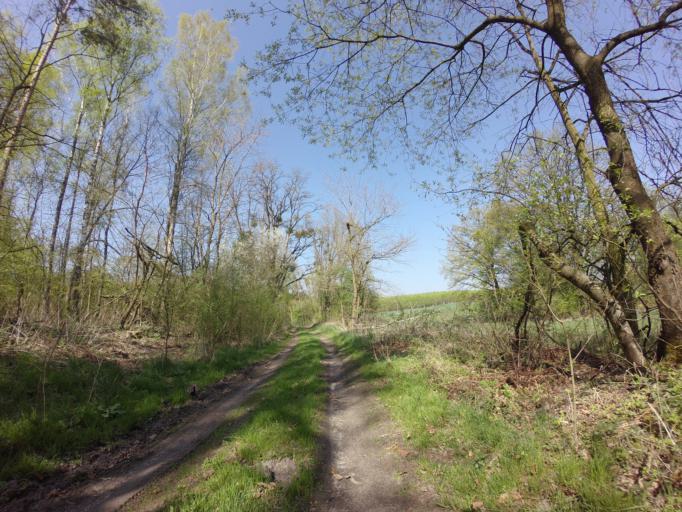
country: PL
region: West Pomeranian Voivodeship
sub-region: Powiat choszczenski
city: Choszczno
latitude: 53.1927
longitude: 15.3697
